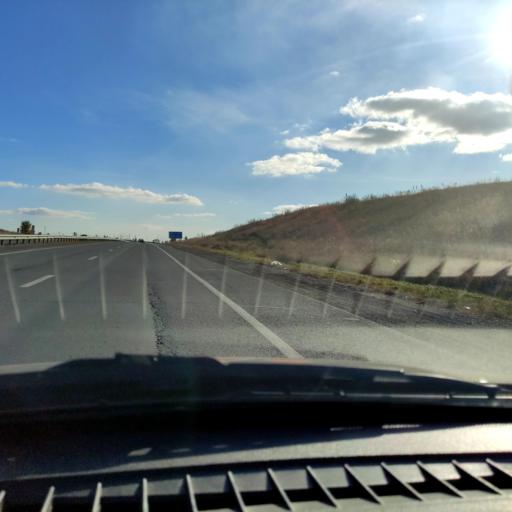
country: RU
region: Samara
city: Zhigulevsk
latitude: 53.5086
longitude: 49.5380
